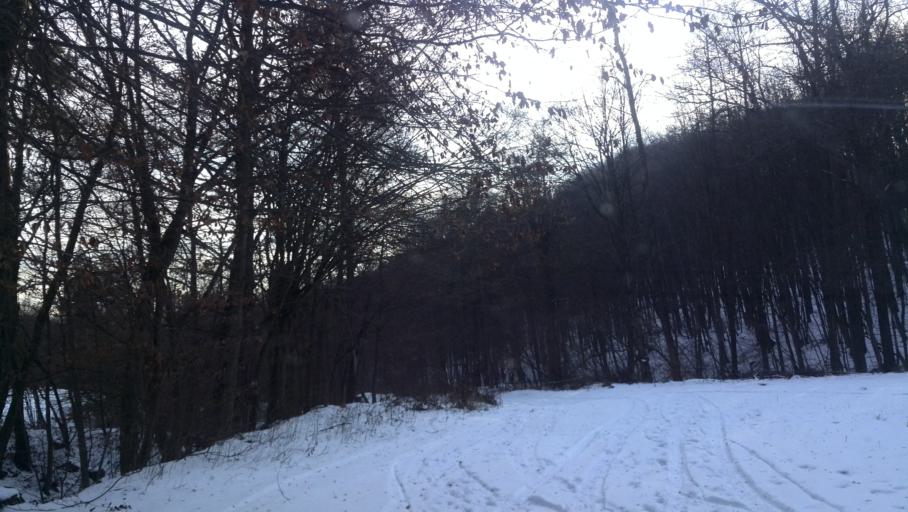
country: SK
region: Presovsky
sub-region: Okres Presov
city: Presov
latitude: 48.9681
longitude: 21.1033
